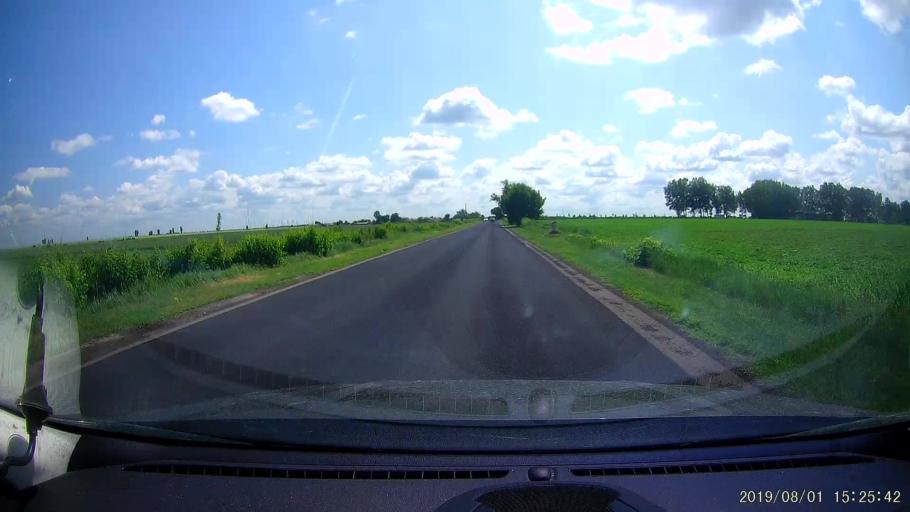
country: RO
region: Braila
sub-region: Comuna Viziru
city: Lanurile
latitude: 45.0186
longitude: 27.7313
